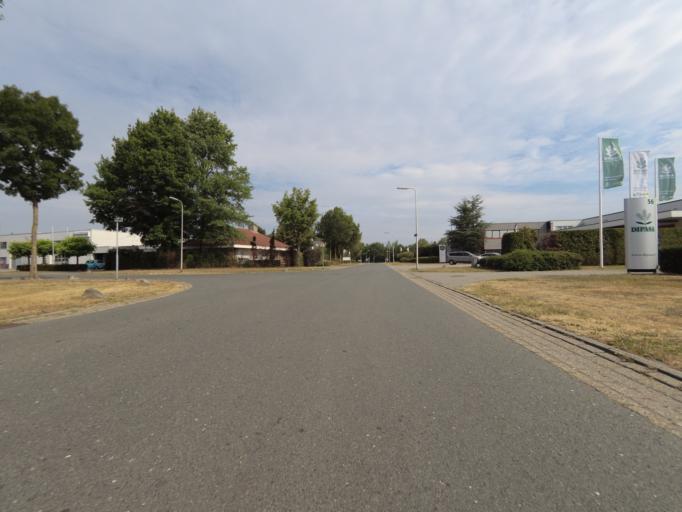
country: NL
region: Overijssel
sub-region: Gemeente Hengelo
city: Hengelo
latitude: 52.2149
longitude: 6.8142
